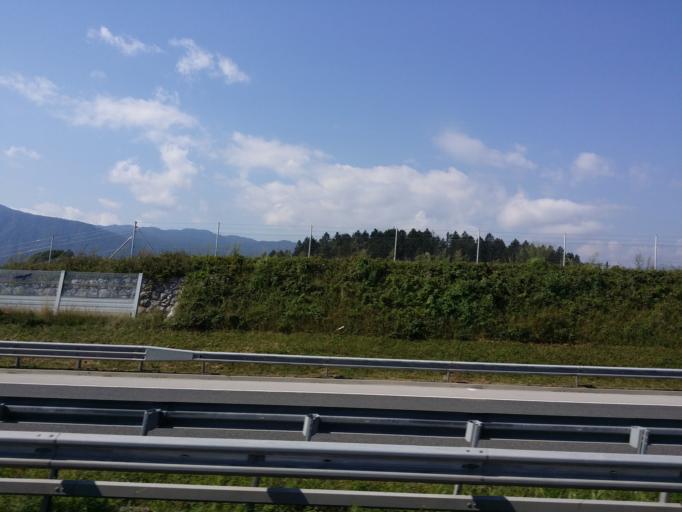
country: SI
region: Radovljica
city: Radovljica
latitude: 46.3500
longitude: 14.1786
